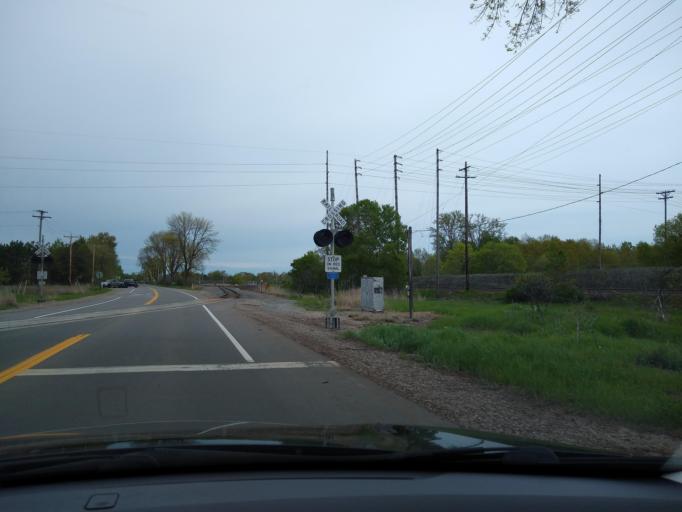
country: US
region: Michigan
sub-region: Delta County
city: Escanaba
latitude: 45.7706
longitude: -87.0692
